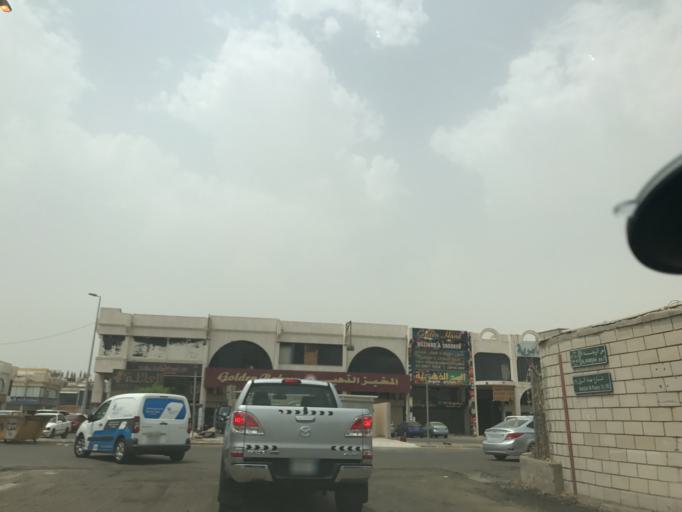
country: SA
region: Makkah
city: Jeddah
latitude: 21.5597
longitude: 39.1694
